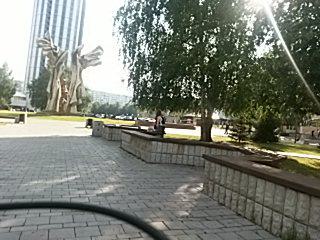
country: RU
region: Tatarstan
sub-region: Tukayevskiy Rayon
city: Naberezhnyye Chelny
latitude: 55.7419
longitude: 52.4159
